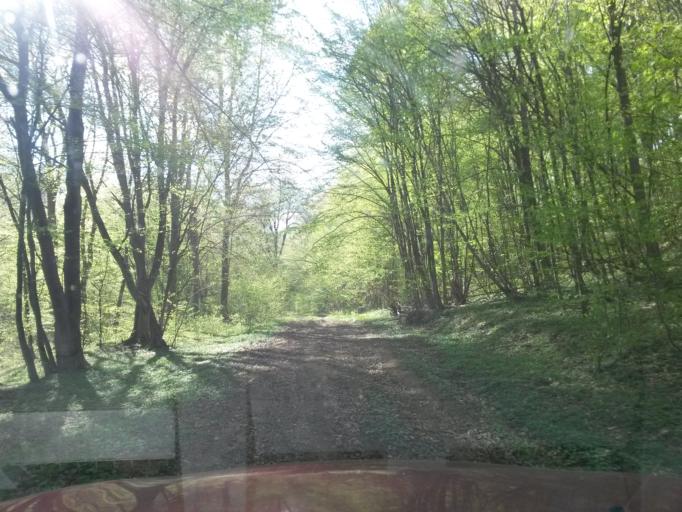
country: SK
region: Presovsky
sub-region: Okres Presov
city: Presov
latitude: 48.9471
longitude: 21.1432
